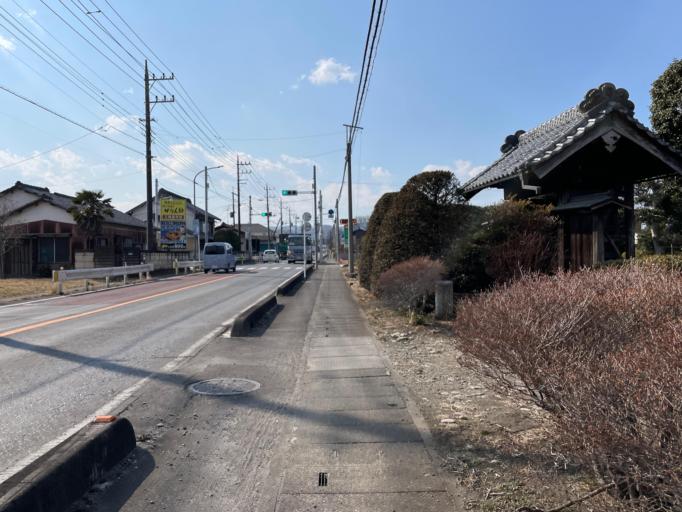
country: JP
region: Saitama
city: Yorii
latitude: 36.1258
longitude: 139.2260
